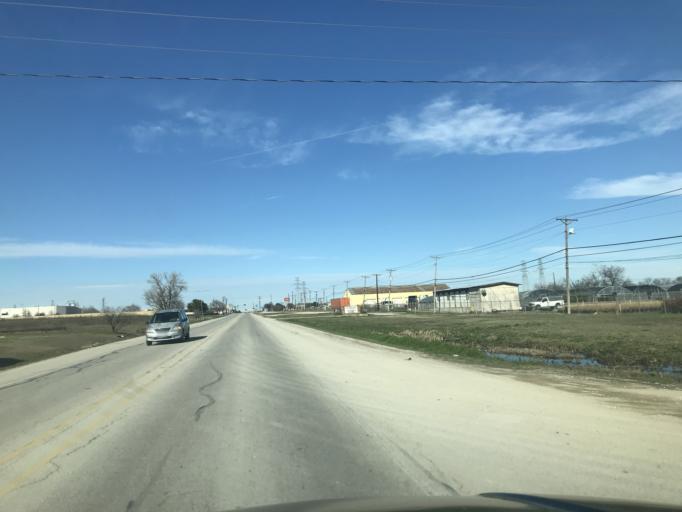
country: US
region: Texas
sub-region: Tarrant County
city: Blue Mound
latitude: 32.8332
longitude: -97.3429
